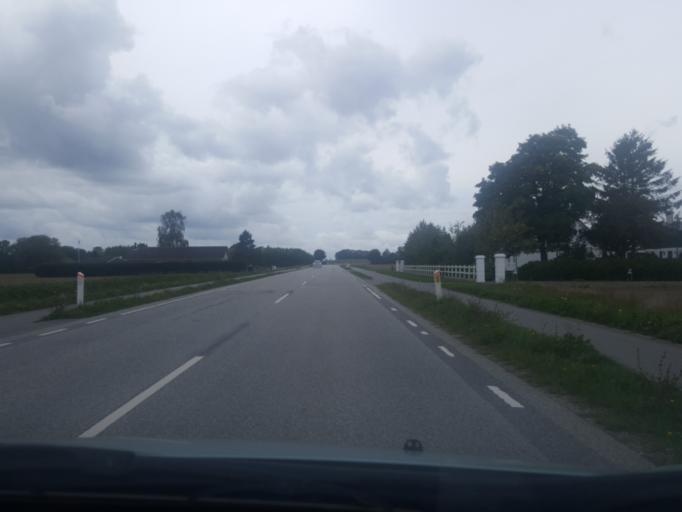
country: DK
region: Zealand
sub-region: Guldborgsund Kommune
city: Nykobing Falster
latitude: 54.7015
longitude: 11.9372
